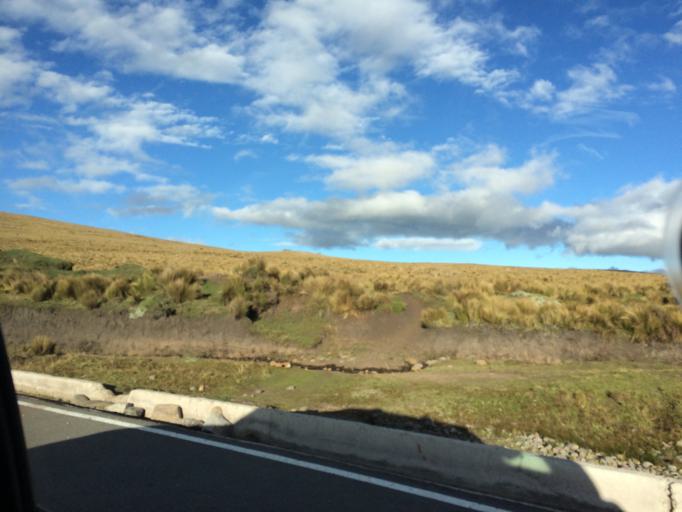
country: EC
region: Chimborazo
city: Alausi
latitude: -2.2250
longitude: -78.6872
